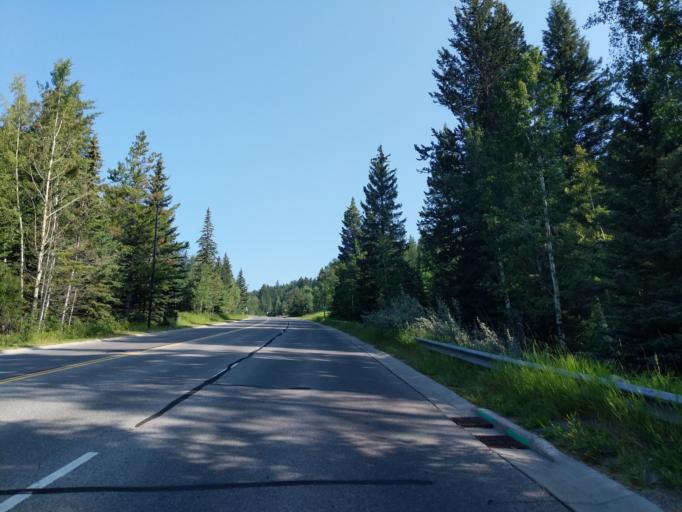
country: CA
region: Alberta
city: Canmore
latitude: 51.0963
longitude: -115.3403
